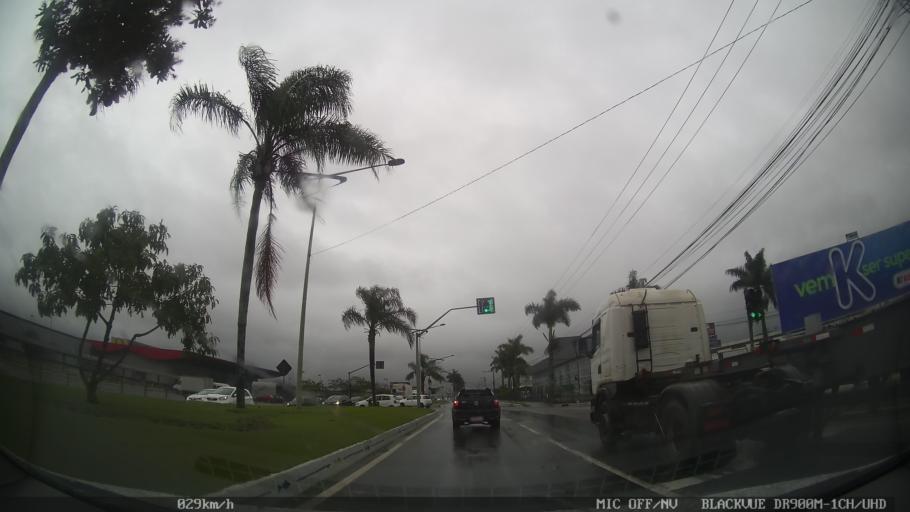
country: BR
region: Santa Catarina
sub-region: Itajai
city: Itajai
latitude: -26.9134
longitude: -48.6938
